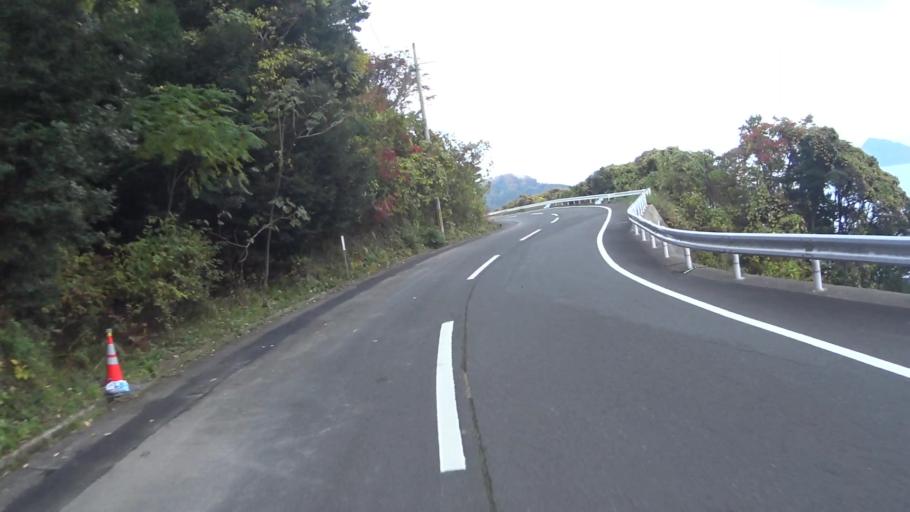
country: JP
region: Kyoto
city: Maizuru
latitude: 35.5709
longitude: 135.4495
